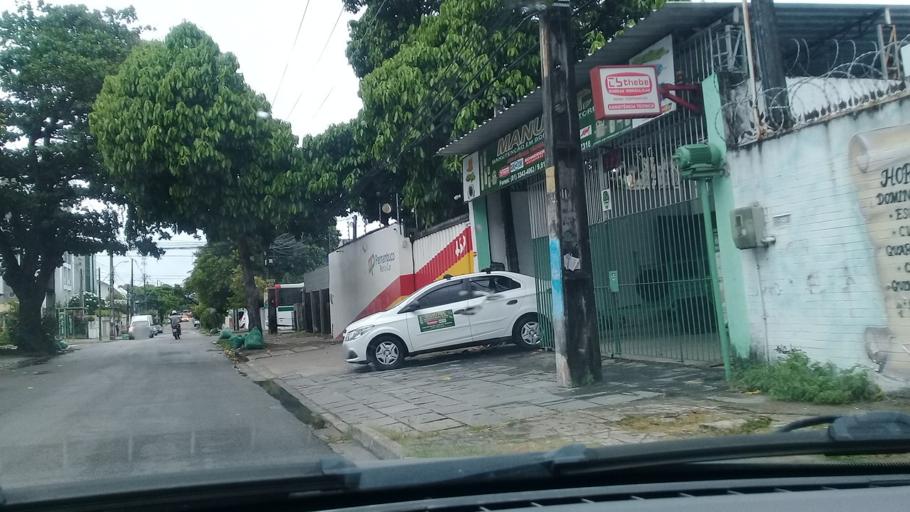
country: BR
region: Pernambuco
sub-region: Recife
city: Recife
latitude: -8.1376
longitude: -34.9142
